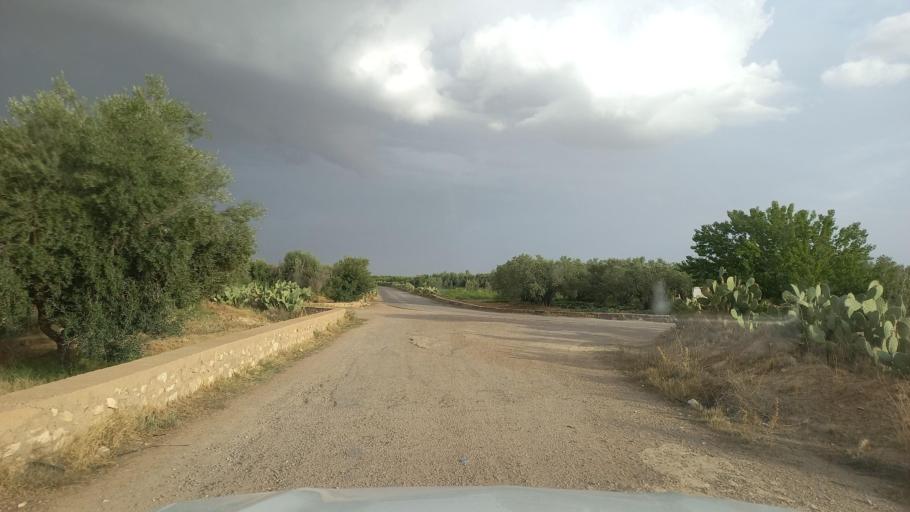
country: TN
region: Al Qasrayn
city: Kasserine
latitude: 35.2814
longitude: 9.0554
